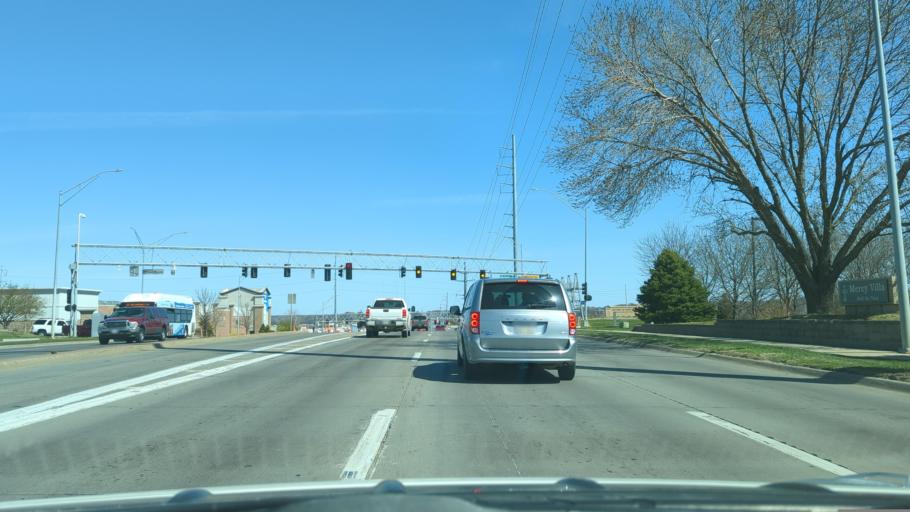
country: US
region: Nebraska
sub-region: Douglas County
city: Ralston
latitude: 41.2426
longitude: -96.0239
